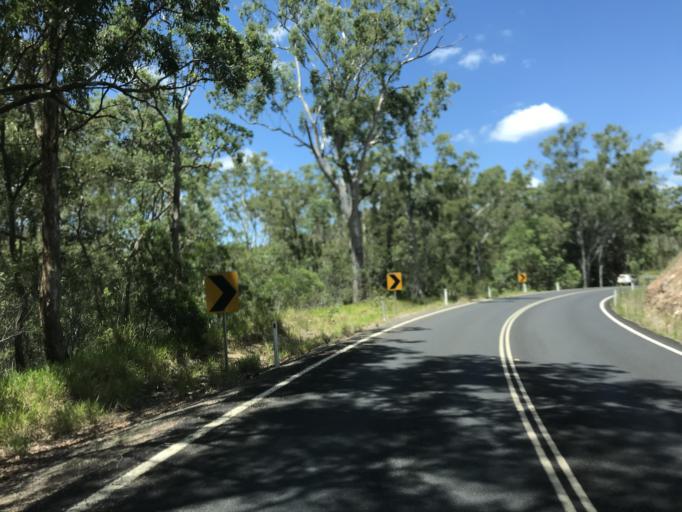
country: AU
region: Queensland
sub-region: Tablelands
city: Atherton
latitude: -17.4049
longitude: 145.3886
